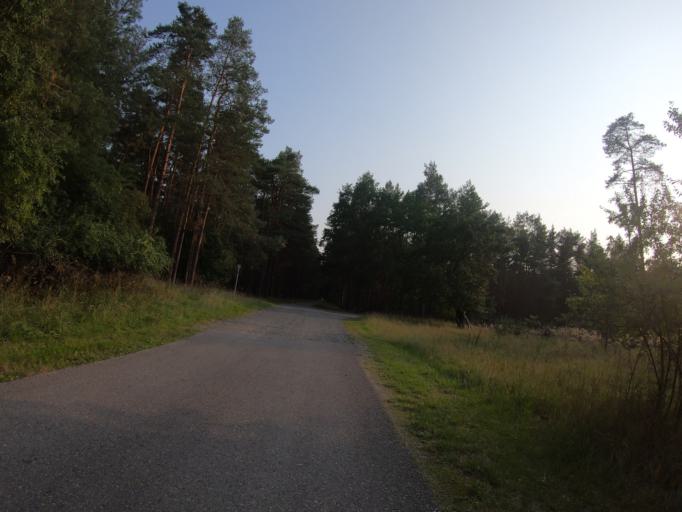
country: DE
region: Lower Saxony
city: Leiferde
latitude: 52.4550
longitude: 10.4491
